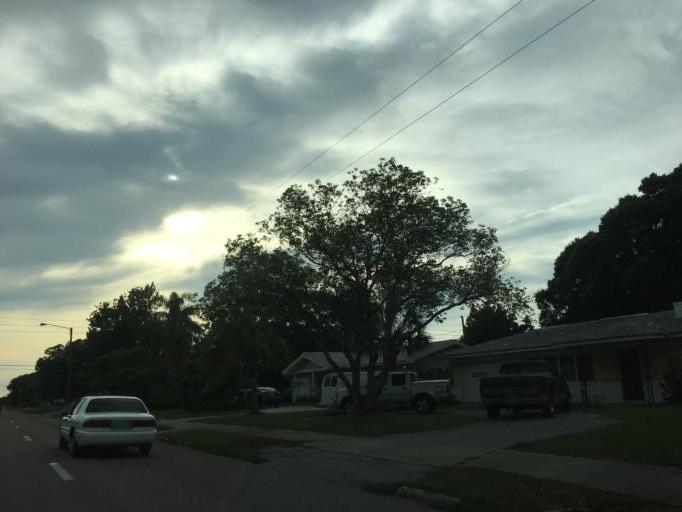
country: US
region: Florida
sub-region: Pinellas County
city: Saint Petersburg
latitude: 27.7919
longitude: -82.6868
